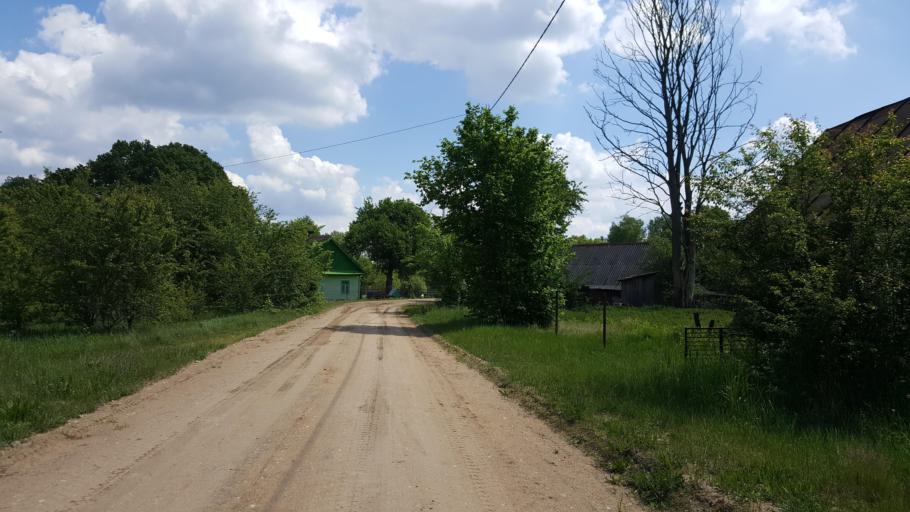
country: BY
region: Brest
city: Kamyanyuki
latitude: 52.4888
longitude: 23.9644
